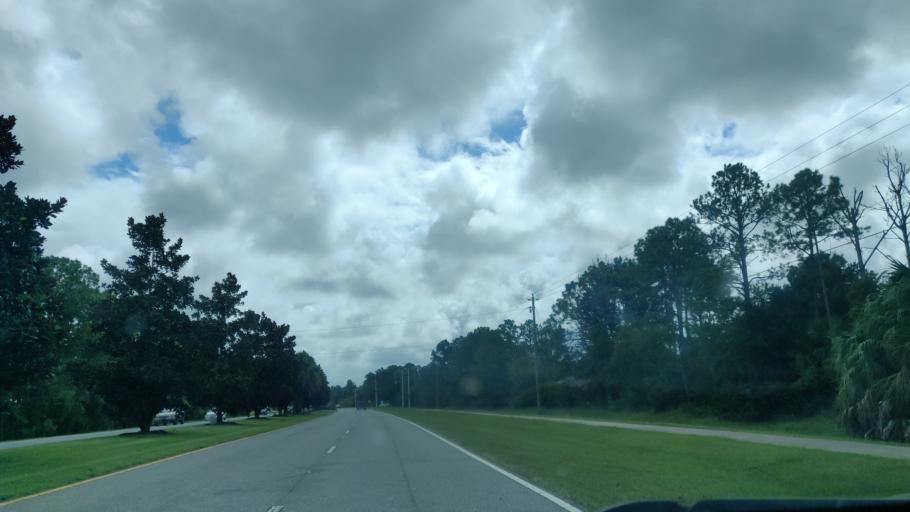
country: US
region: Florida
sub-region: Flagler County
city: Bunnell
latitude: 29.5207
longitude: -81.2251
